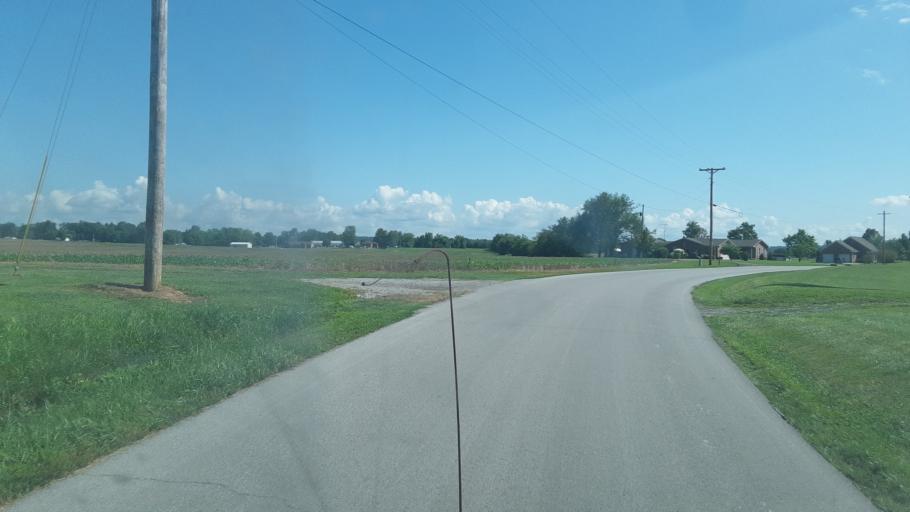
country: US
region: Kentucky
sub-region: Todd County
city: Elkton
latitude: 36.8095
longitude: -87.1830
